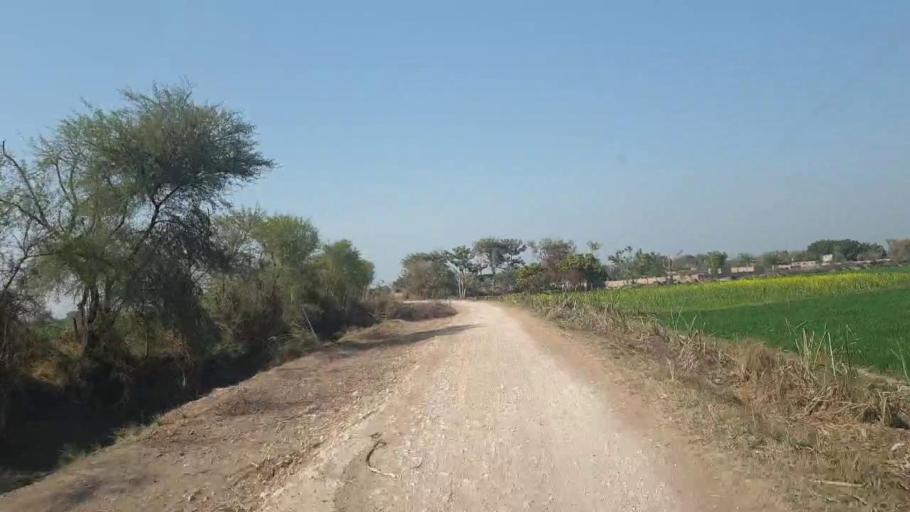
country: PK
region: Sindh
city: Shahdadpur
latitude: 26.0497
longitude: 68.4630
